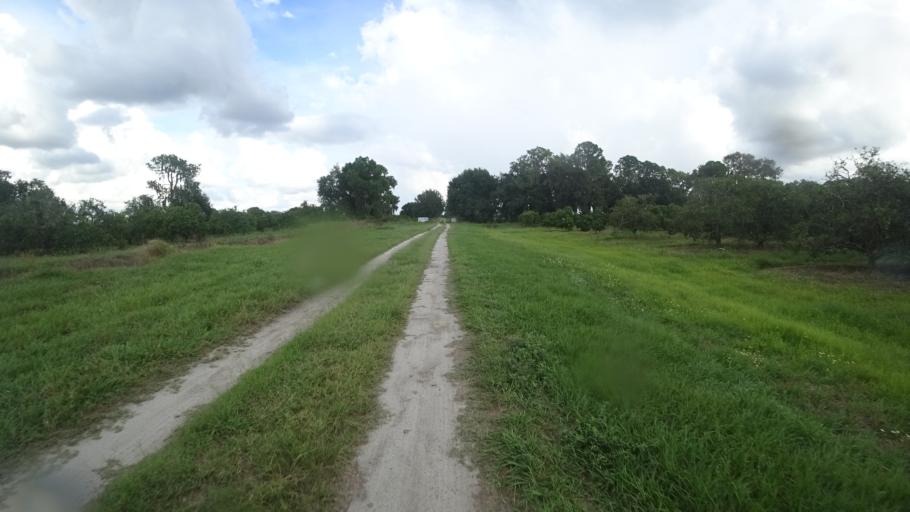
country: US
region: Florida
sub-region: Hillsborough County
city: Wimauma
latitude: 27.5741
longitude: -82.1029
